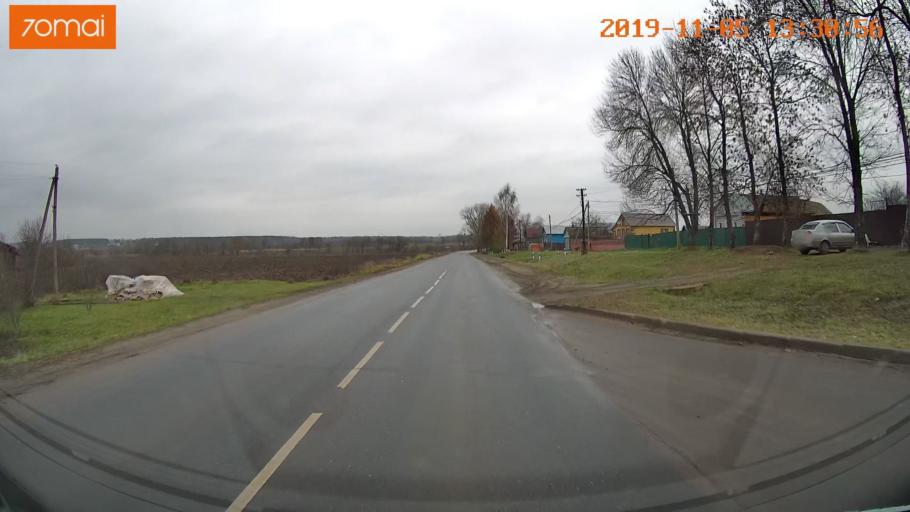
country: RU
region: Ivanovo
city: Shuya
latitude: 56.8707
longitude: 41.3932
